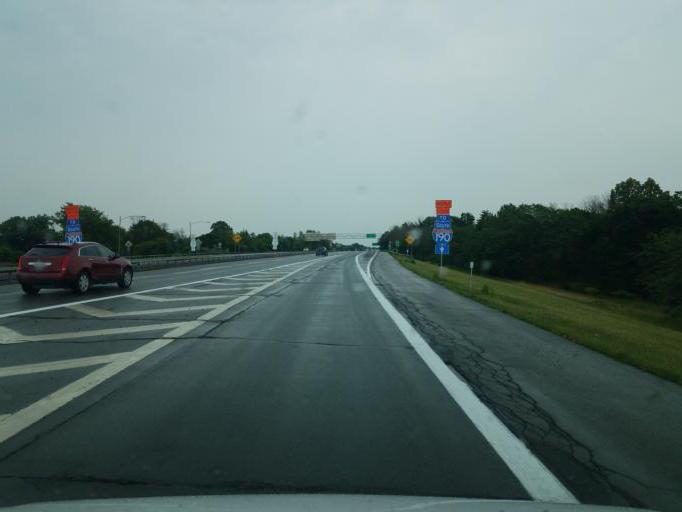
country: US
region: New York
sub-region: Niagara County
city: Niagara Falls
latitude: 43.0802
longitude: -78.9857
